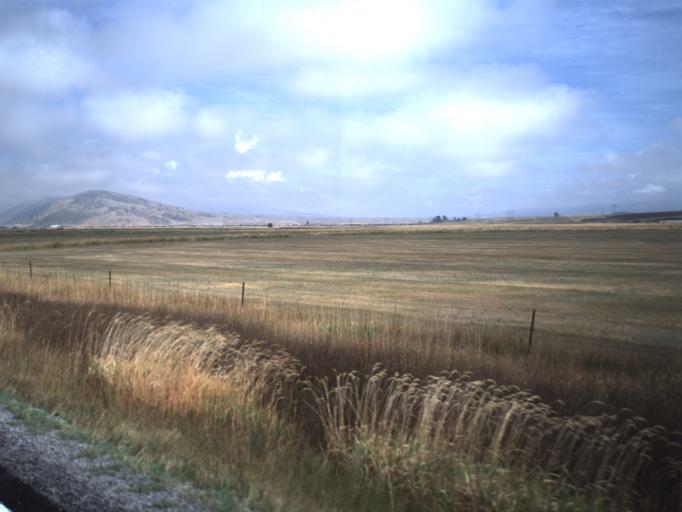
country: US
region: Utah
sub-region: Rich County
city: Randolph
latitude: 41.4964
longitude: -111.1214
